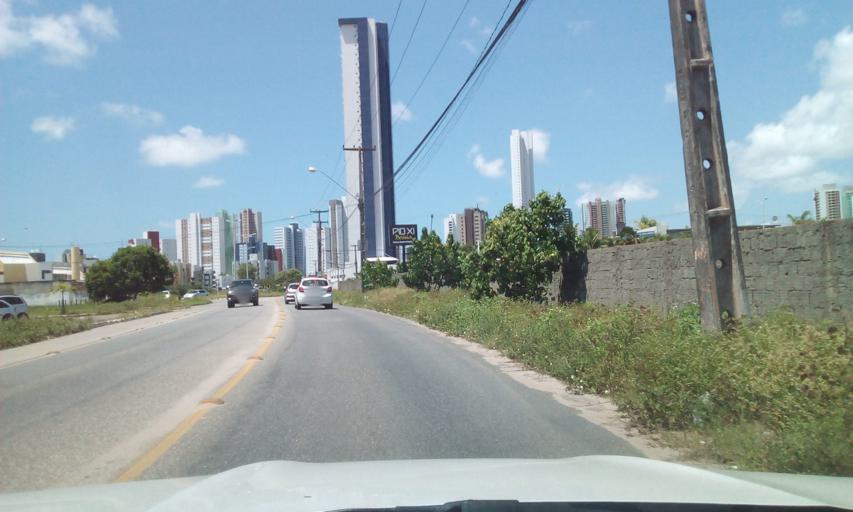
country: BR
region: Paraiba
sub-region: Joao Pessoa
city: Joao Pessoa
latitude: -7.0757
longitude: -34.8415
